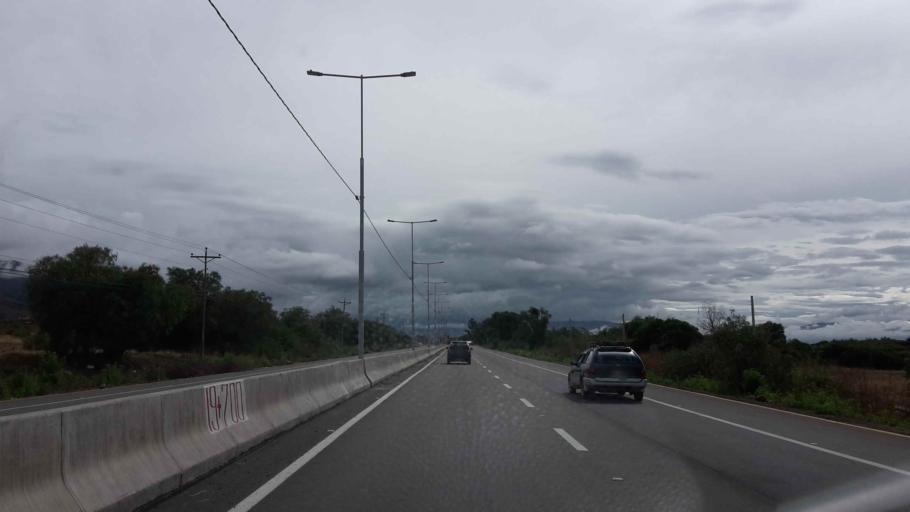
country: BO
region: Cochabamba
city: Tarata
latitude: -17.5432
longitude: -66.0002
